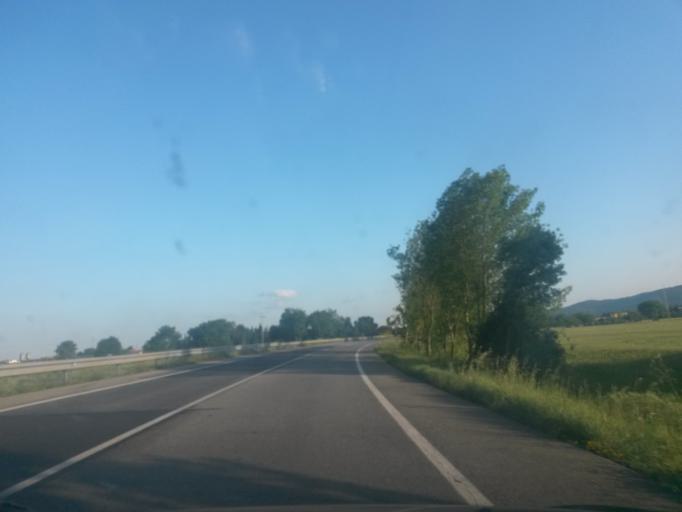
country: ES
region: Catalonia
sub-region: Provincia de Girona
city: Banyoles
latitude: 42.1499
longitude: 2.7622
